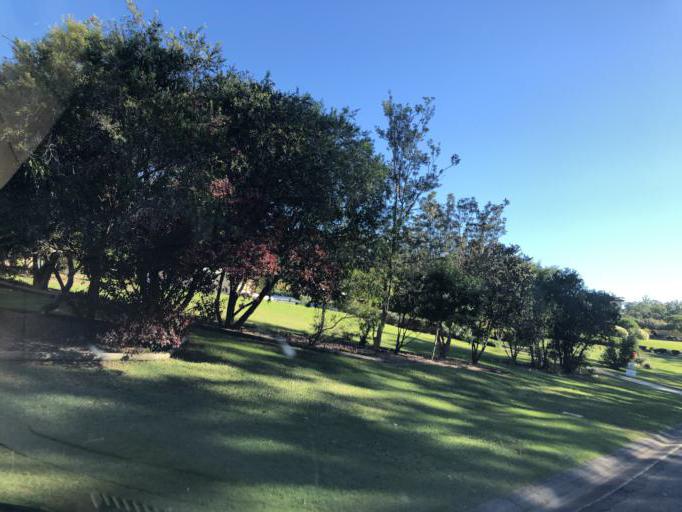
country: AU
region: New South Wales
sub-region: Nambucca Shire
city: Macksville
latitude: -30.6781
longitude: 152.9556
